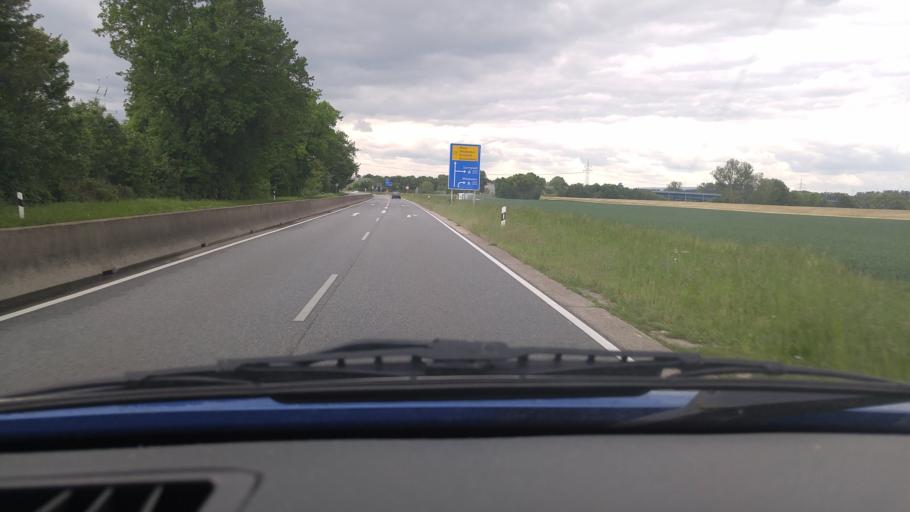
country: DE
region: Hesse
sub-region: Regierungsbezirk Darmstadt
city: Bischofsheim
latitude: 49.9949
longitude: 8.3529
